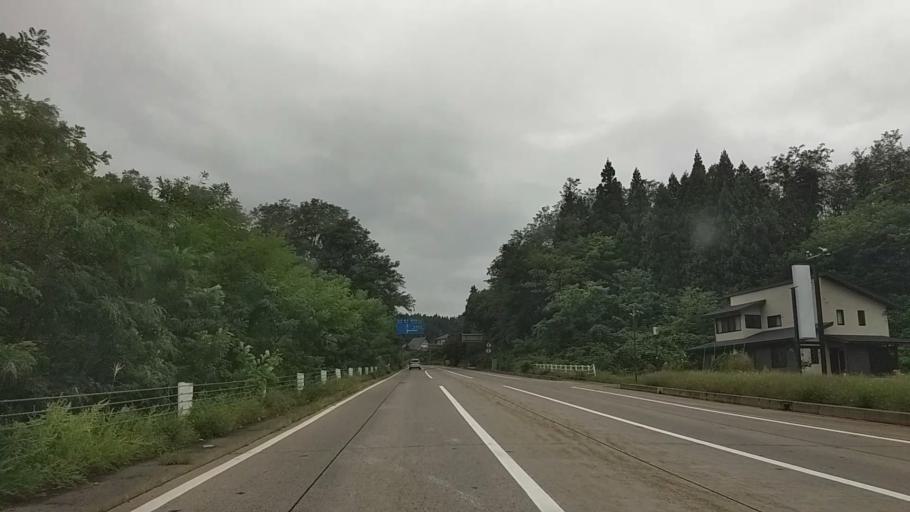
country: JP
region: Nagano
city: Iiyama
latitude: 36.8207
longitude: 138.3472
